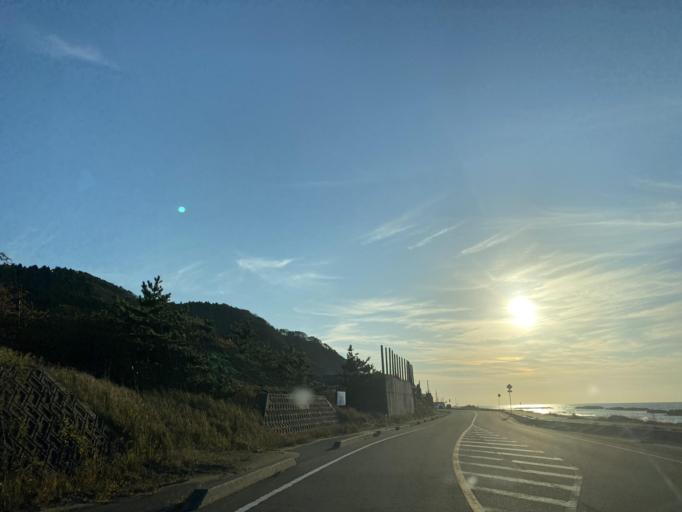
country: JP
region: Niigata
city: Kashiwazaki
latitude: 37.4987
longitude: 138.6417
